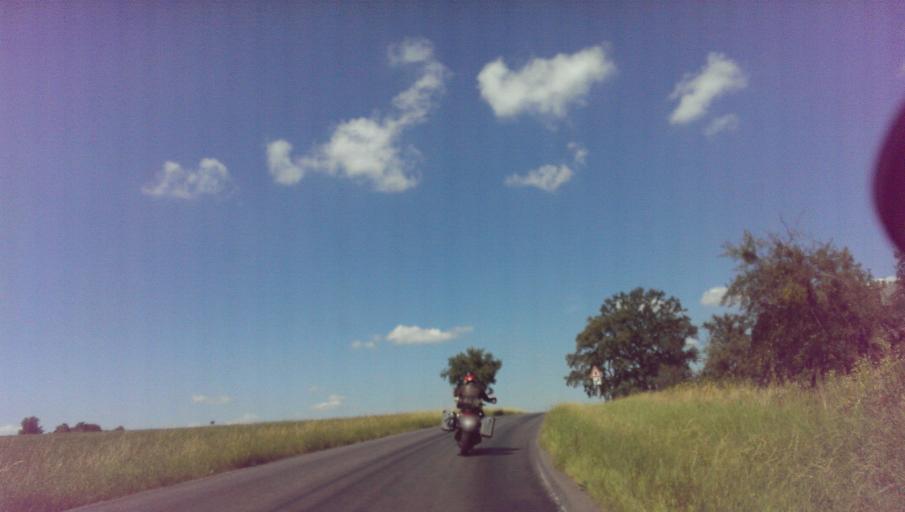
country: CZ
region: Moravskoslezsky
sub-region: Okres Novy Jicin
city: Pribor
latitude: 49.6283
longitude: 18.1794
